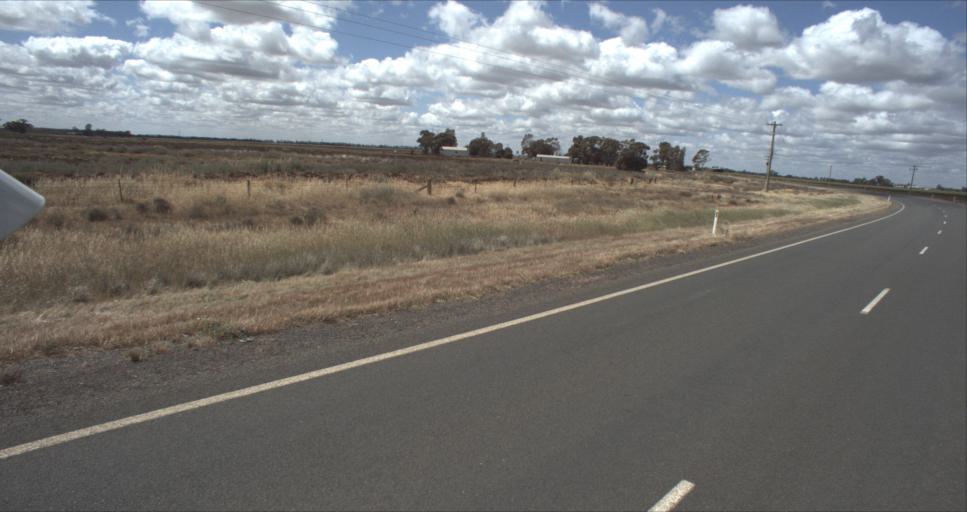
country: AU
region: New South Wales
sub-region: Murrumbidgee Shire
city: Darlington Point
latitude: -34.4932
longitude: 146.1670
